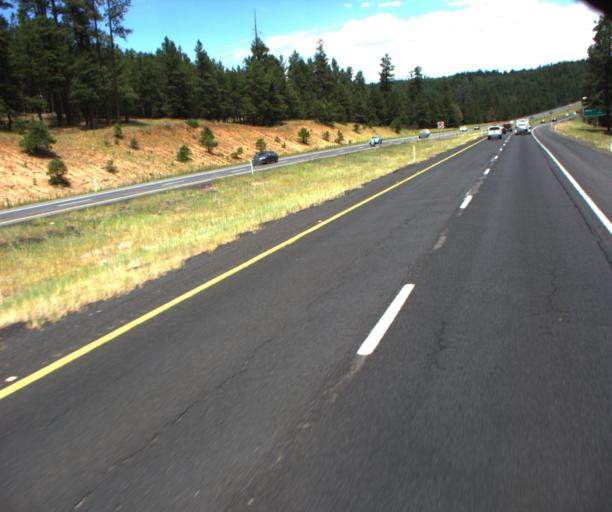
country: US
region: Arizona
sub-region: Coconino County
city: Mountainaire
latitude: 35.0374
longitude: -111.6844
